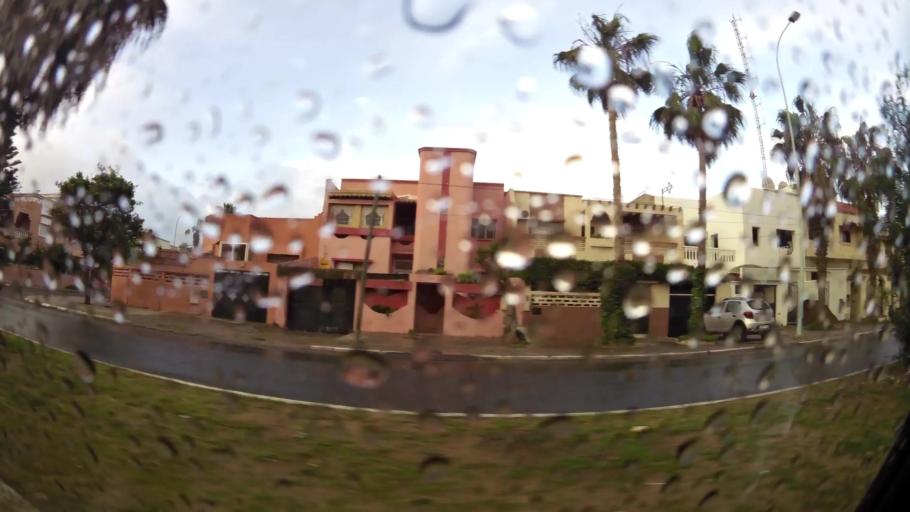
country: MA
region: Doukkala-Abda
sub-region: El-Jadida
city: El Jadida
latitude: 33.2314
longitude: -8.4991
